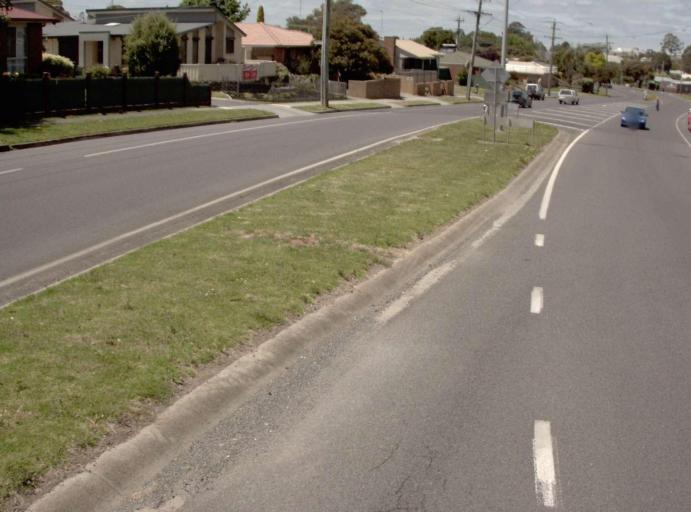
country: AU
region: Victoria
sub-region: Baw Baw
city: Warragul
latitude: -38.4801
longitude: 145.9493
